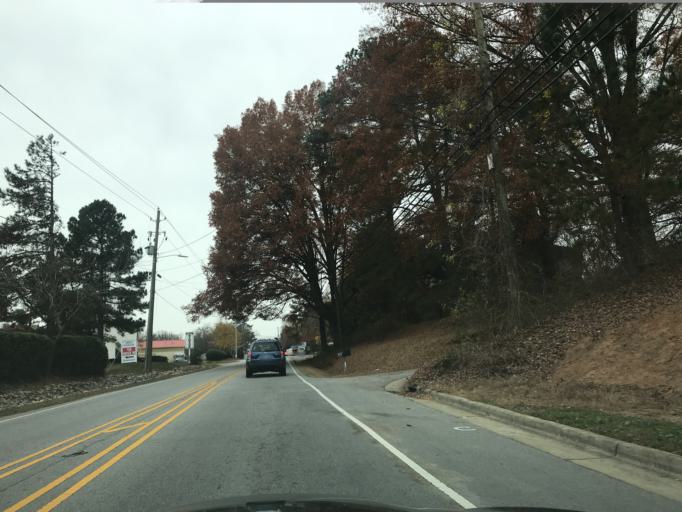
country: US
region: North Carolina
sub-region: Wake County
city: Raleigh
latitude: 35.8518
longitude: -78.6045
